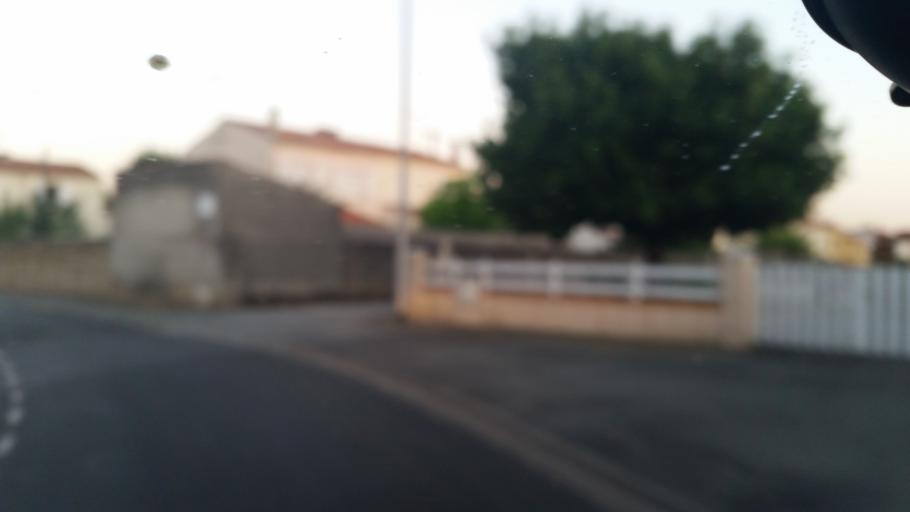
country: FR
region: Poitou-Charentes
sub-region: Departement de la Charente-Maritime
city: Marans
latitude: 46.3076
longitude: -1.0001
